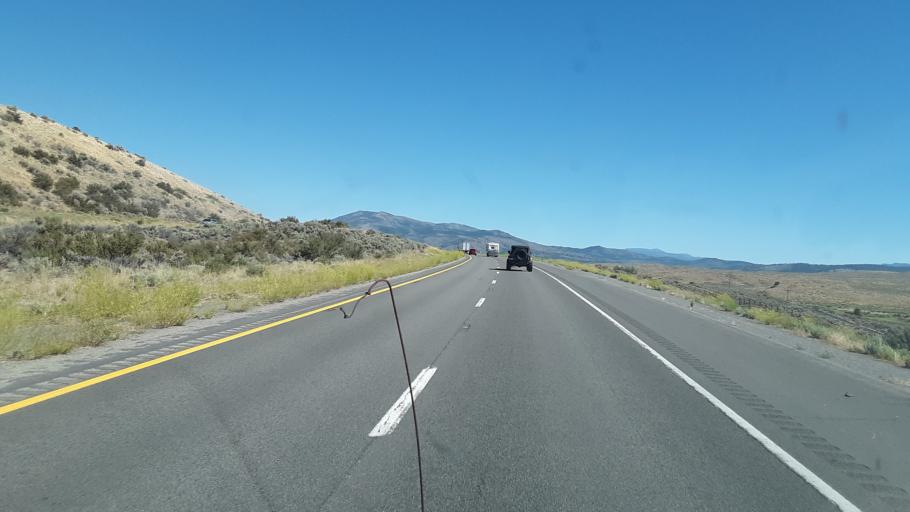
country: US
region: Nevada
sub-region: Washoe County
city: Cold Springs
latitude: 39.7029
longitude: -120.0333
